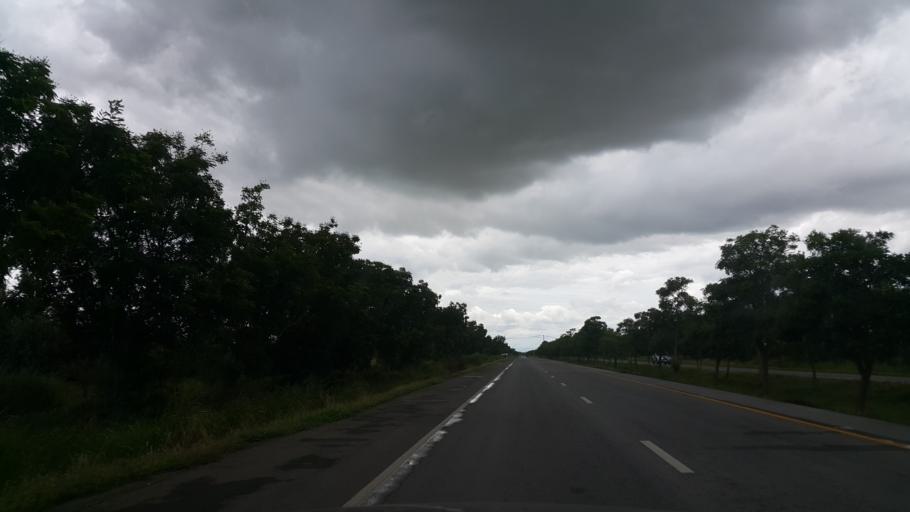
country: TH
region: Sukhothai
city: Ban Na
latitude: 17.0657
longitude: 99.7804
